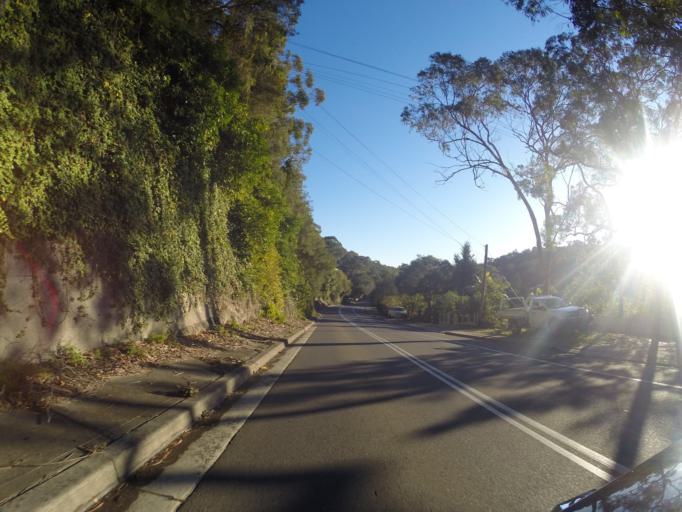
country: AU
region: New South Wales
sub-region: Sutherland Shire
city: Grays Point
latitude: -34.0553
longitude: 151.0765
